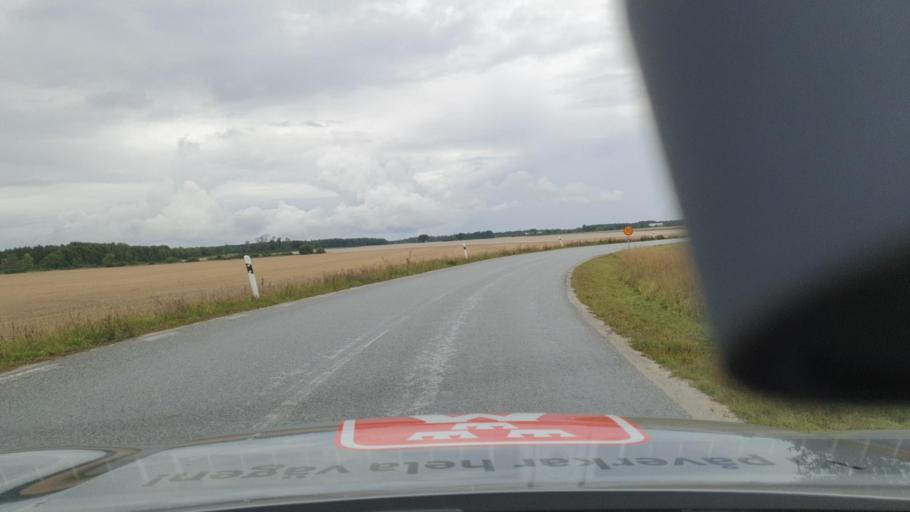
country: SE
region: Gotland
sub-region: Gotland
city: Visby
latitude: 57.5018
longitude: 18.4311
